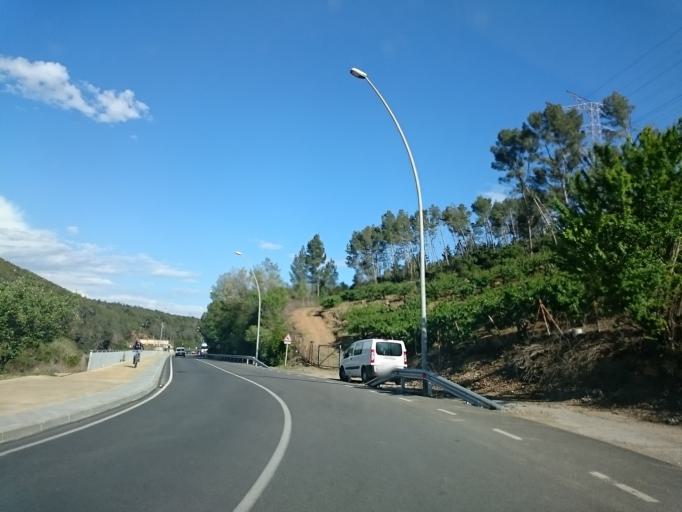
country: ES
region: Catalonia
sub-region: Provincia de Barcelona
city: Viladecans
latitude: 41.3310
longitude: 2.0028
